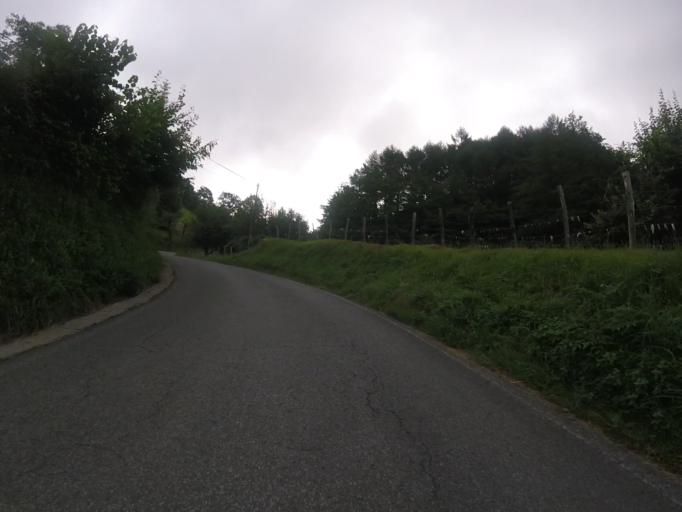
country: ES
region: Navarre
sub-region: Provincia de Navarra
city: Leitza
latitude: 43.0852
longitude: -1.9004
